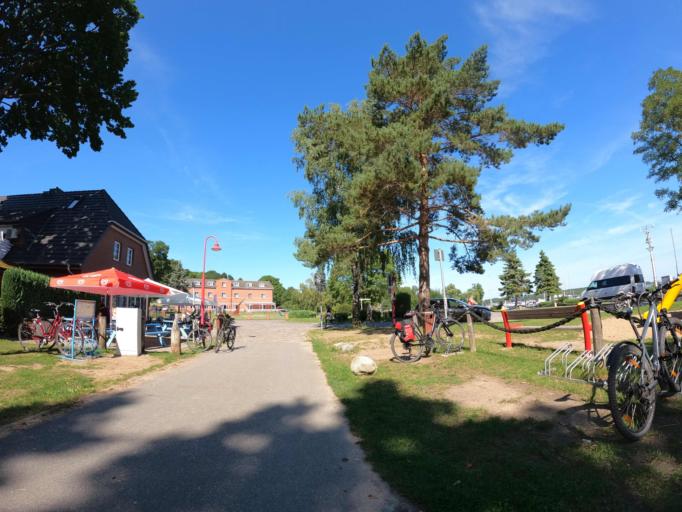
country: DE
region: Mecklenburg-Vorpommern
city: Prohn
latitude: 54.4331
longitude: 13.0306
